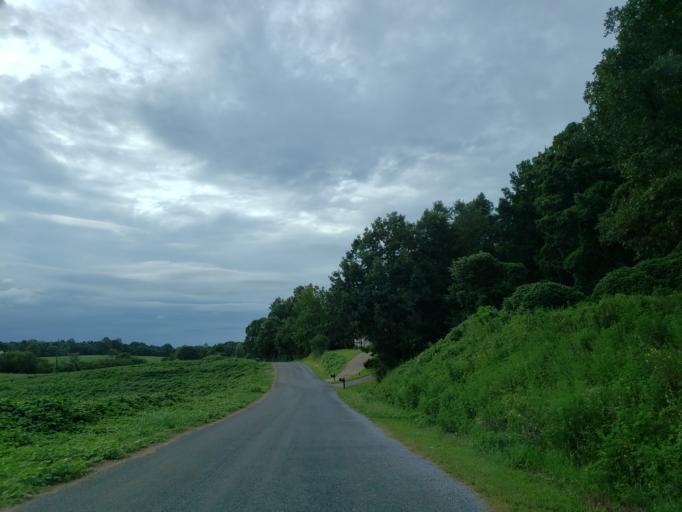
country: US
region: Georgia
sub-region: Pickens County
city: Jasper
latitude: 34.4717
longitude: -84.5098
